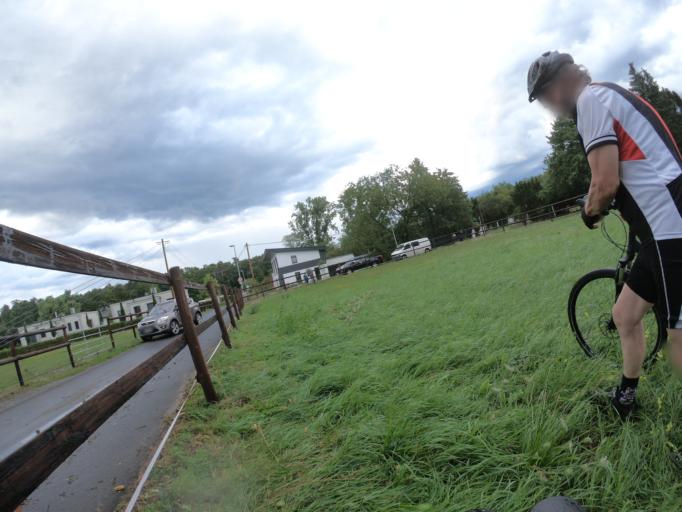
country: DE
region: Hesse
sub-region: Regierungsbezirk Darmstadt
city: Egelsbach
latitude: 49.9782
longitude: 8.6519
